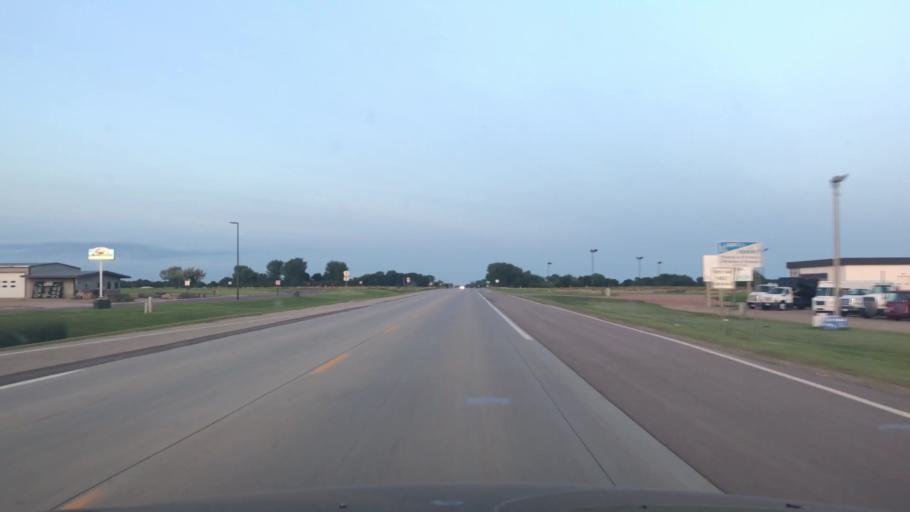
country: US
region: Minnesota
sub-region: Redwood County
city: Redwood Falls
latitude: 44.5413
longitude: -95.0768
